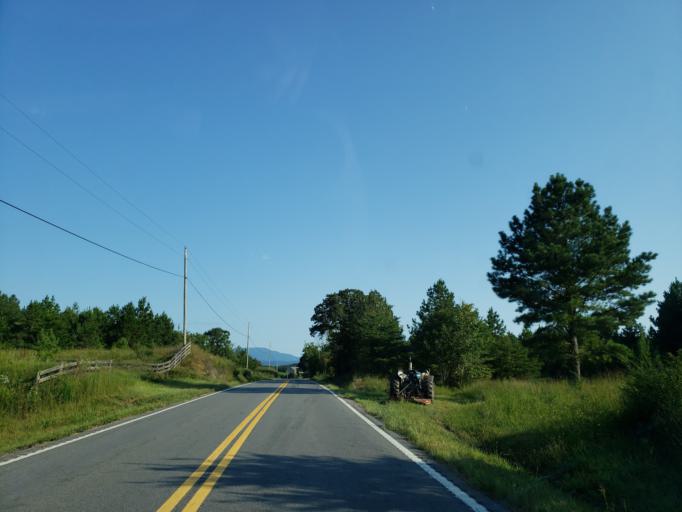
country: US
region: Tennessee
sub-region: Bradley County
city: Wildwood Lake
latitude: 35.0209
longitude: -84.7941
